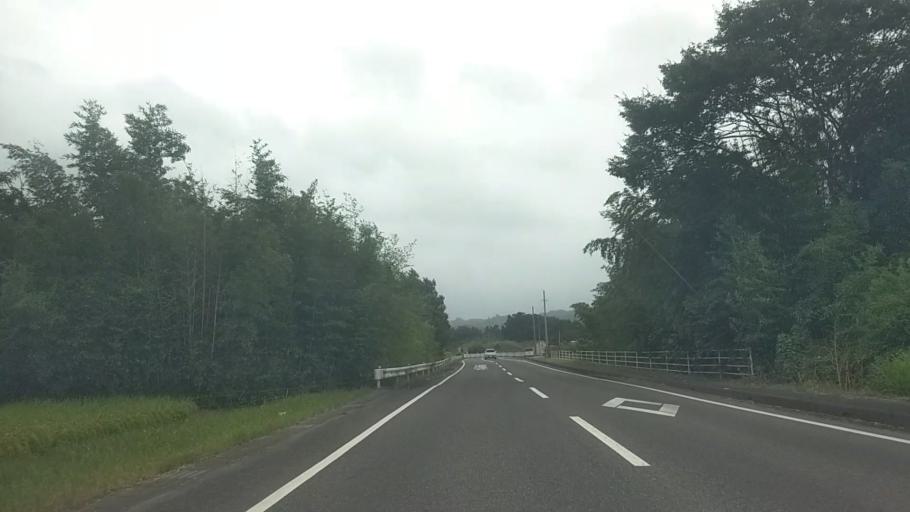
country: JP
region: Chiba
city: Kimitsu
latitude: 35.2188
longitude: 139.9171
